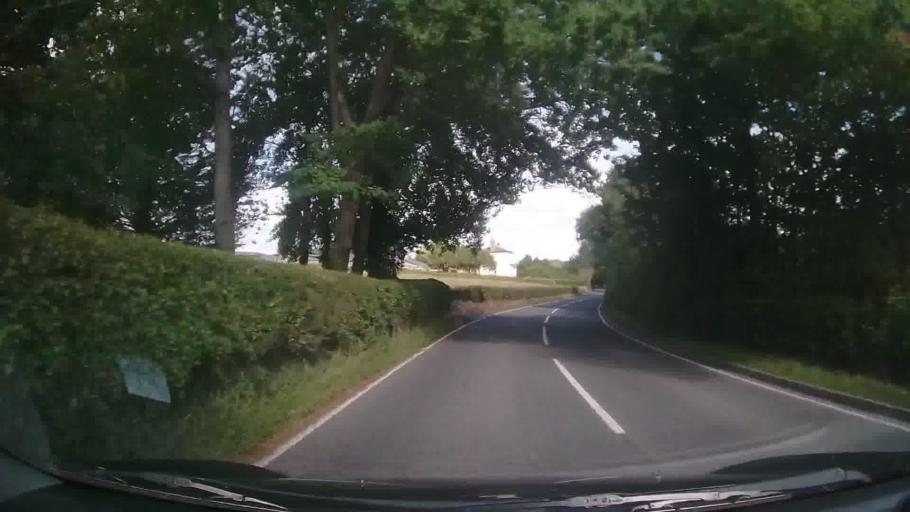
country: GB
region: England
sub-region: Herefordshire
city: Kington
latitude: 52.1890
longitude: -3.0218
